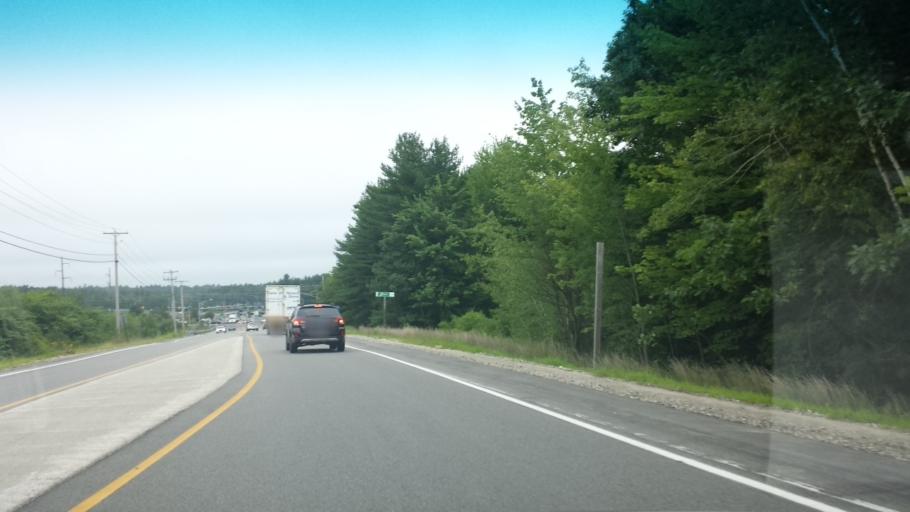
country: US
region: Maine
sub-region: York County
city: Biddeford
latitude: 43.4756
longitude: -70.4941
